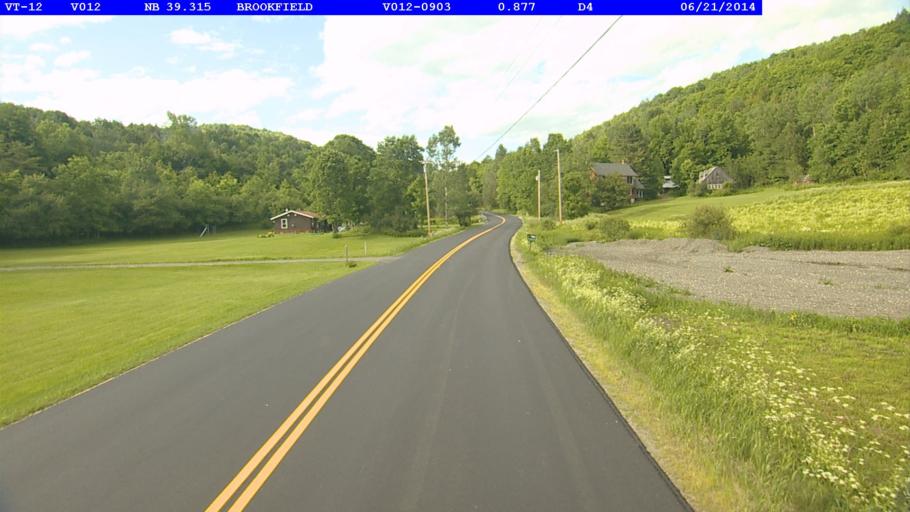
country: US
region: Vermont
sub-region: Orange County
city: Randolph
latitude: 44.0171
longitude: -72.6585
